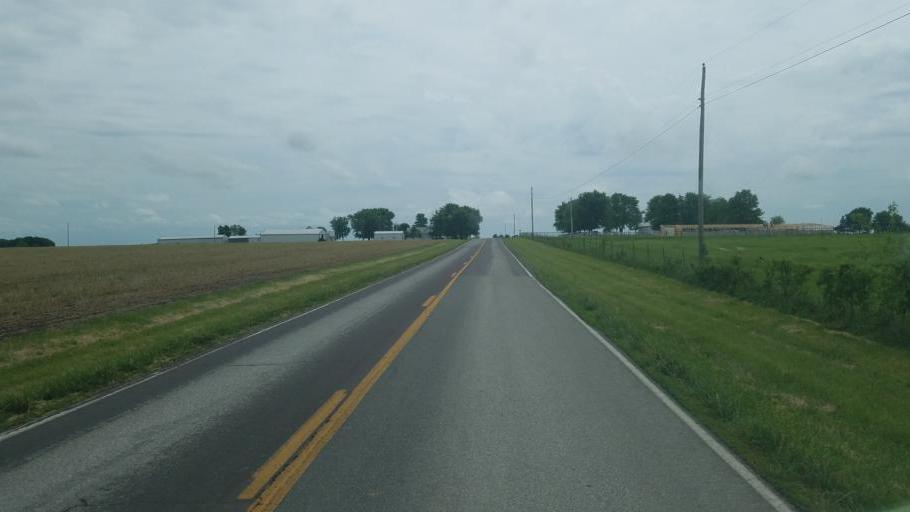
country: US
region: Missouri
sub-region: Morgan County
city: Versailles
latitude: 38.5170
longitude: -92.7431
